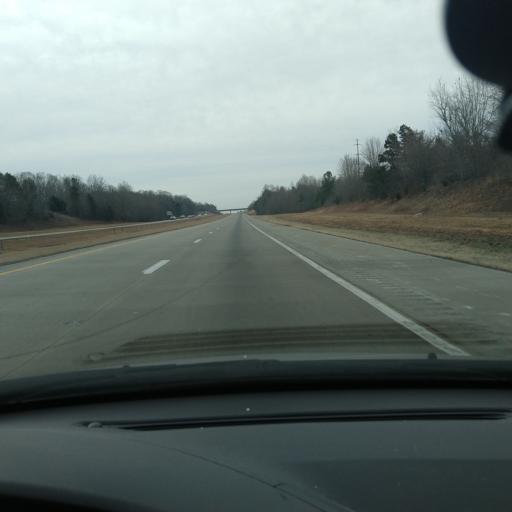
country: US
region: North Carolina
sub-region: Davidson County
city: Midway
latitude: 35.9262
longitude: -80.2318
